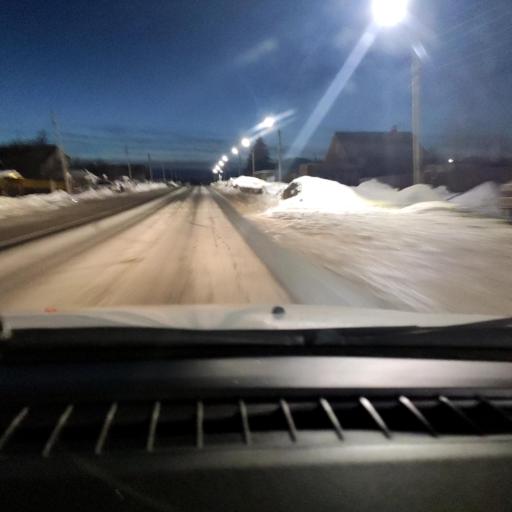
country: RU
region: Samara
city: Kinel'
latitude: 53.2688
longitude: 50.5855
